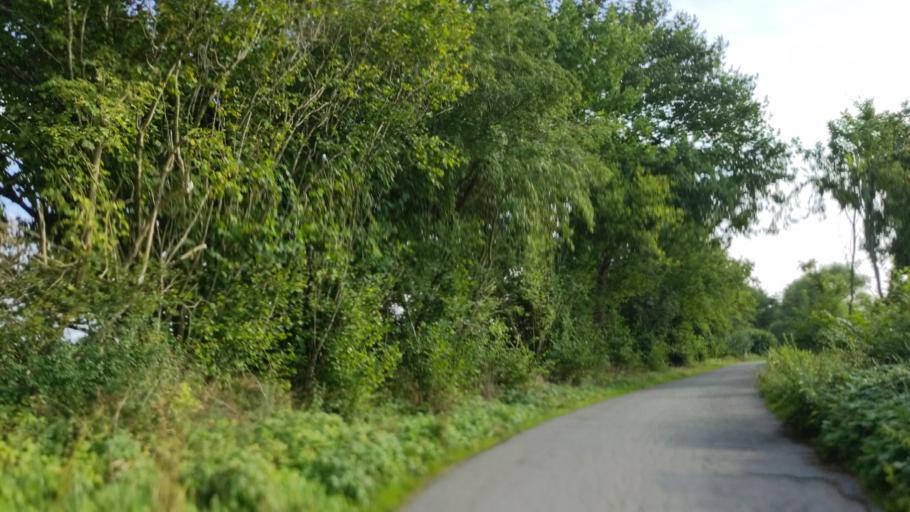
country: DE
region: Schleswig-Holstein
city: Eutin
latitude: 54.1030
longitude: 10.5948
